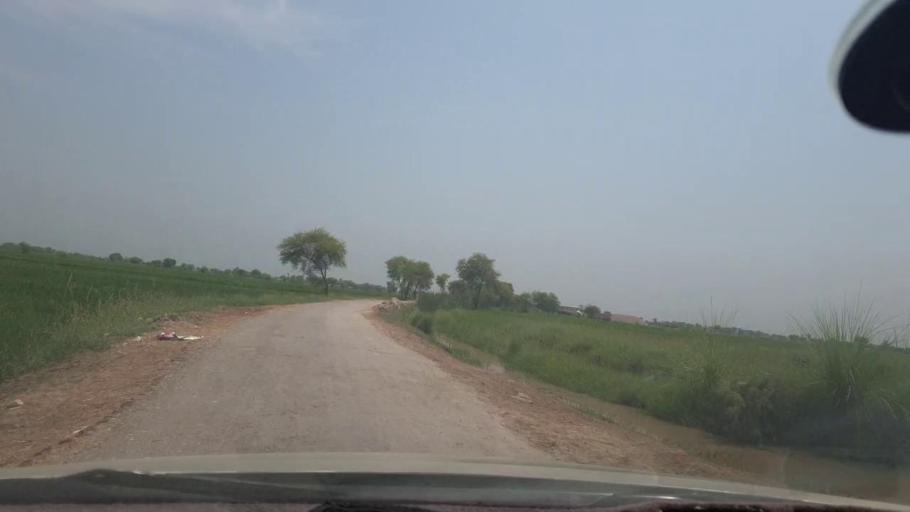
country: PK
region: Sindh
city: Jacobabad
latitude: 28.1793
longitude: 68.3807
